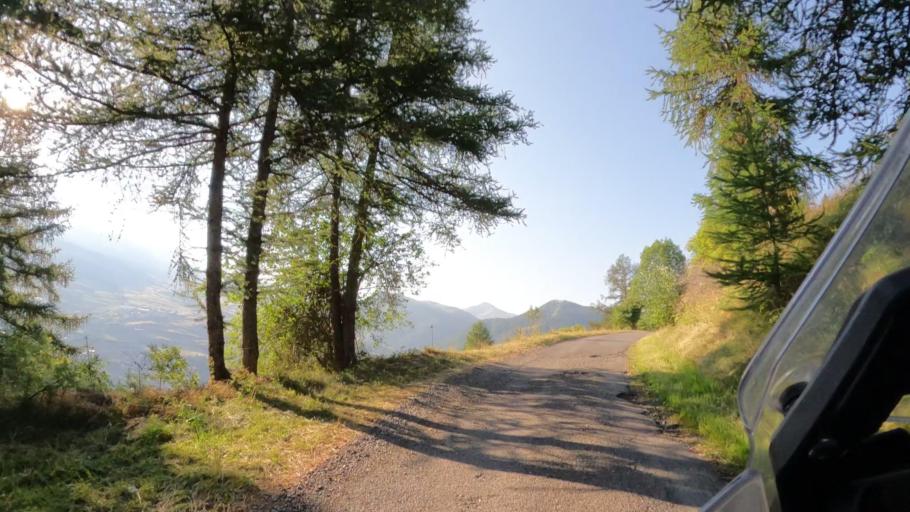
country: FR
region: Provence-Alpes-Cote d'Azur
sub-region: Departement des Hautes-Alpes
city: Guillestre
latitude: 44.6013
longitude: 6.6822
